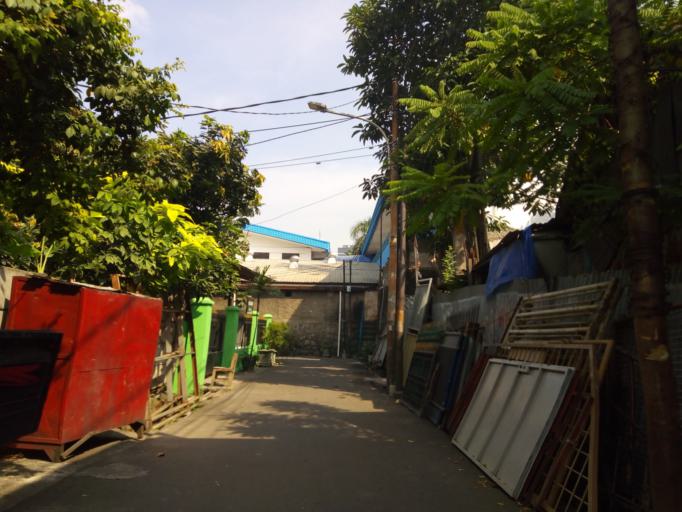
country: ID
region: Jakarta Raya
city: Jakarta
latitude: -6.2052
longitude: 106.8313
